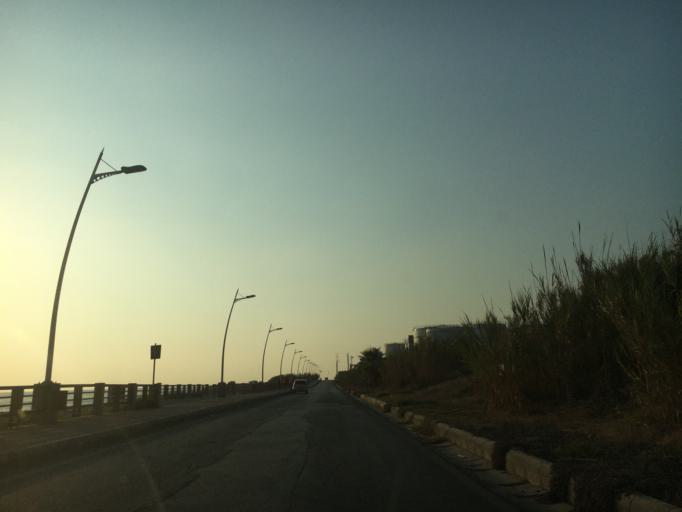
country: LB
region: Mont-Liban
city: Jbail
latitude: 34.1396
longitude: 35.6324
